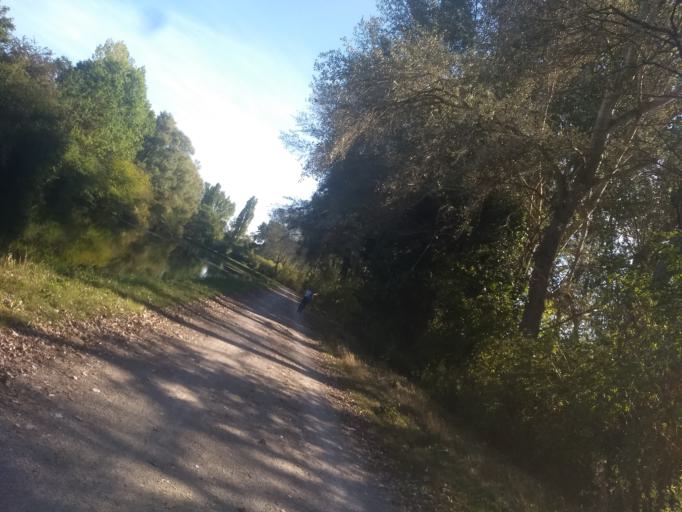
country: FR
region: Nord-Pas-de-Calais
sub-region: Departement du Pas-de-Calais
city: Roeux
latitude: 50.2931
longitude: 2.8873
